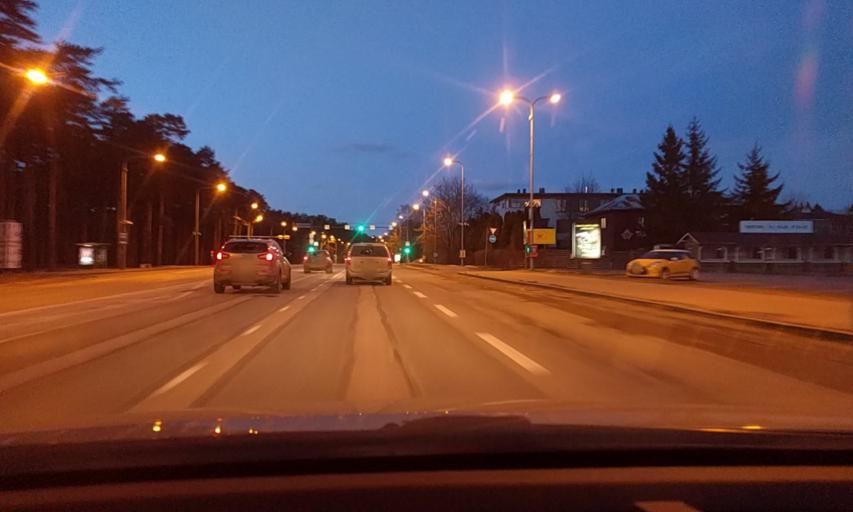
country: EE
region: Harju
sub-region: Viimsi vald
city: Viimsi
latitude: 59.4698
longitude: 24.8350
